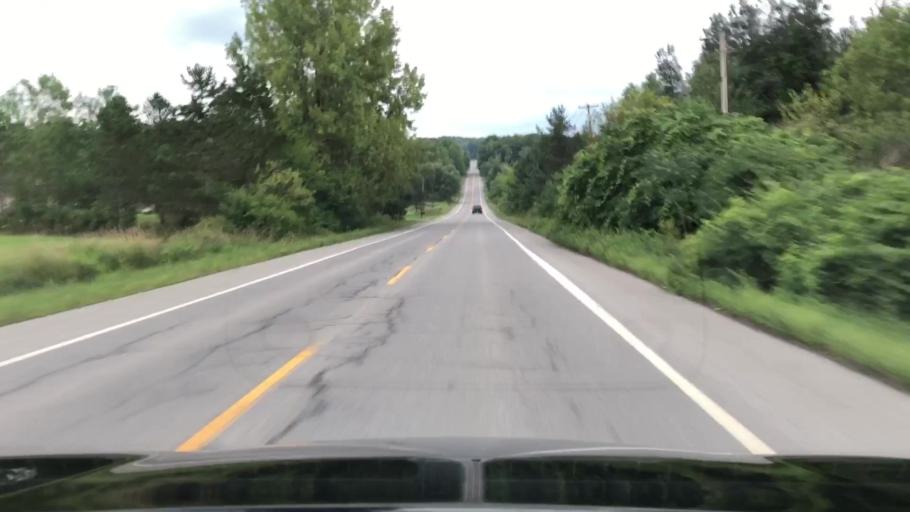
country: US
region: New York
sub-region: Erie County
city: Orchard Park
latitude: 42.7643
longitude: -78.6969
